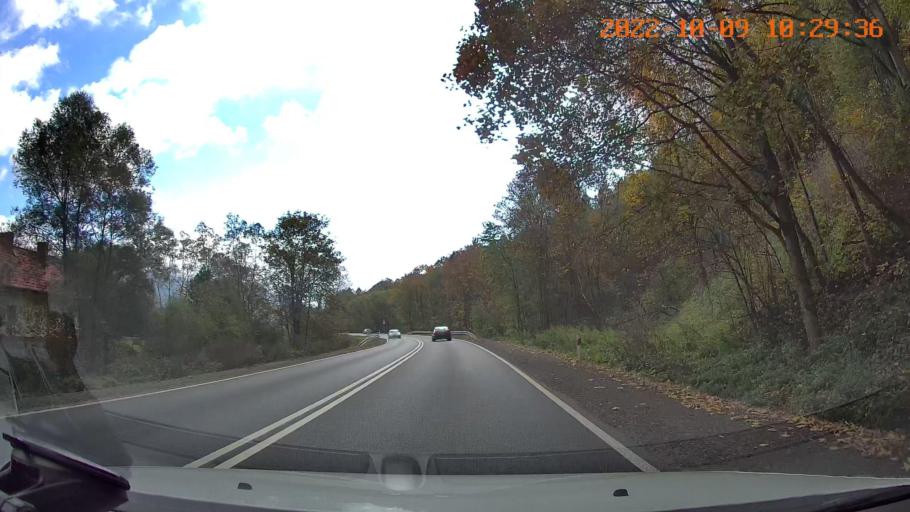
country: PL
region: Lesser Poland Voivodeship
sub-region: Powiat myslenicki
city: Lubien
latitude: 49.7114
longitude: 20.0035
